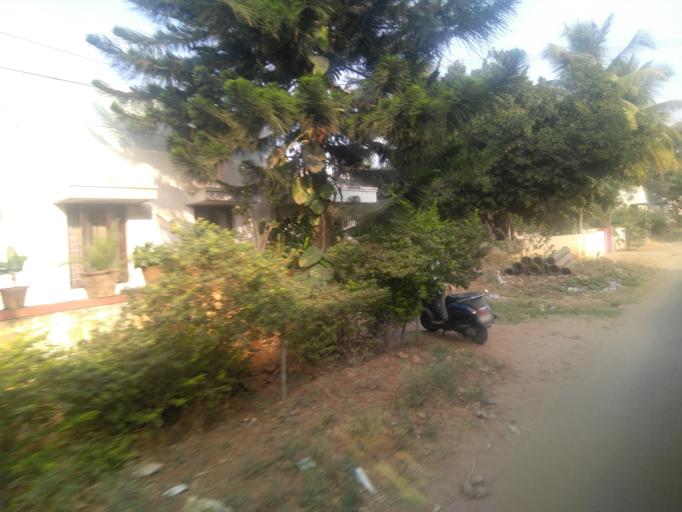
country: IN
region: Tamil Nadu
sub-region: Coimbatore
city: Perur
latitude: 11.0323
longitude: 76.8913
